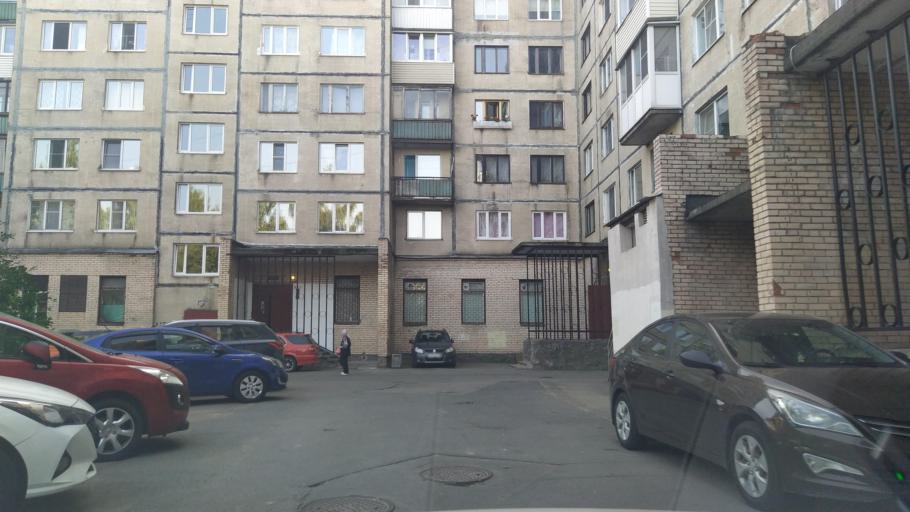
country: RU
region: Leningrad
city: Bugry
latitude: 60.0489
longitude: 30.3803
